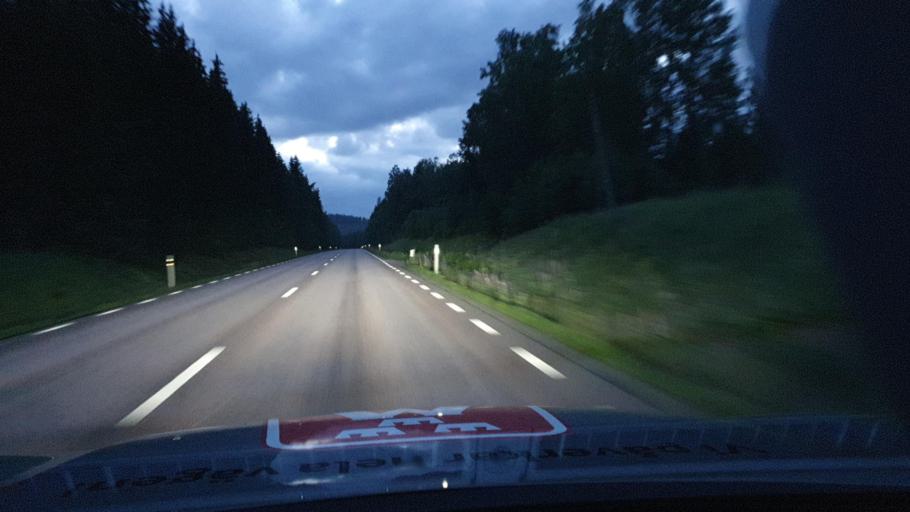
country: SE
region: Vaermland
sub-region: Storfors Kommun
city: Storfors
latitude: 59.4437
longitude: 14.3991
